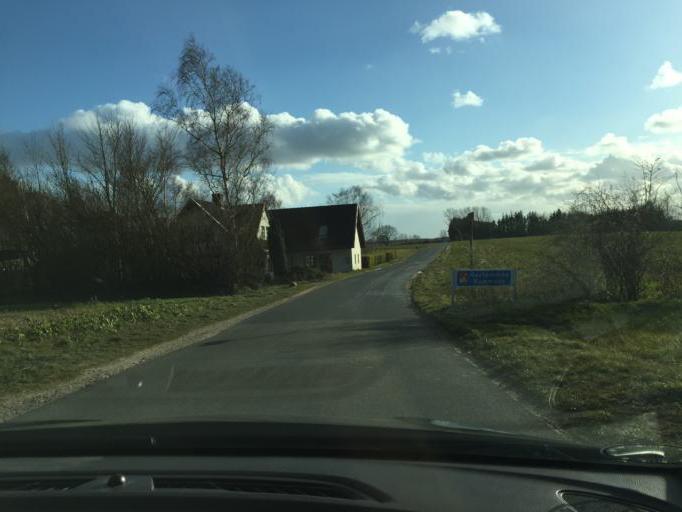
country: DK
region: South Denmark
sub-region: Nyborg Kommune
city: Ullerslev
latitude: 55.3561
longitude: 10.6268
